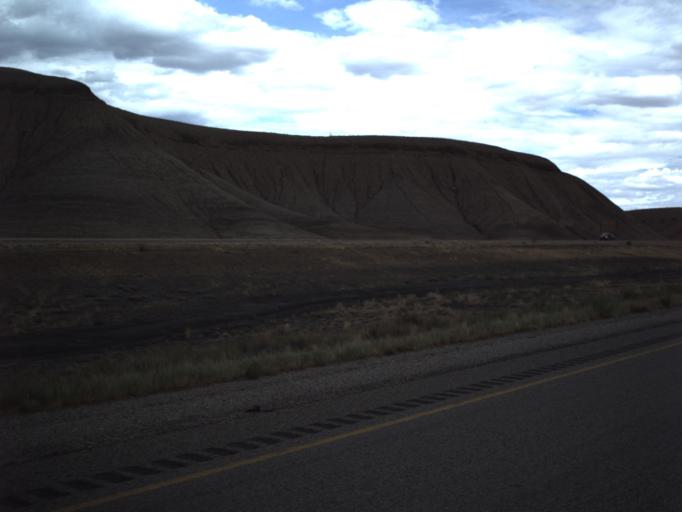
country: US
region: Utah
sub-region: Carbon County
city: East Carbon City
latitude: 38.9709
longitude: -110.0999
